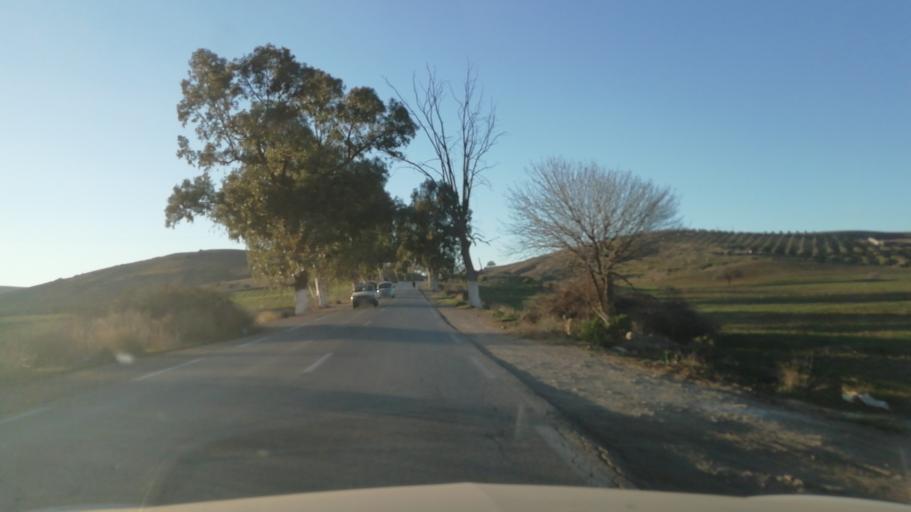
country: DZ
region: Tlemcen
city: Nedroma
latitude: 34.8268
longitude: -1.6564
